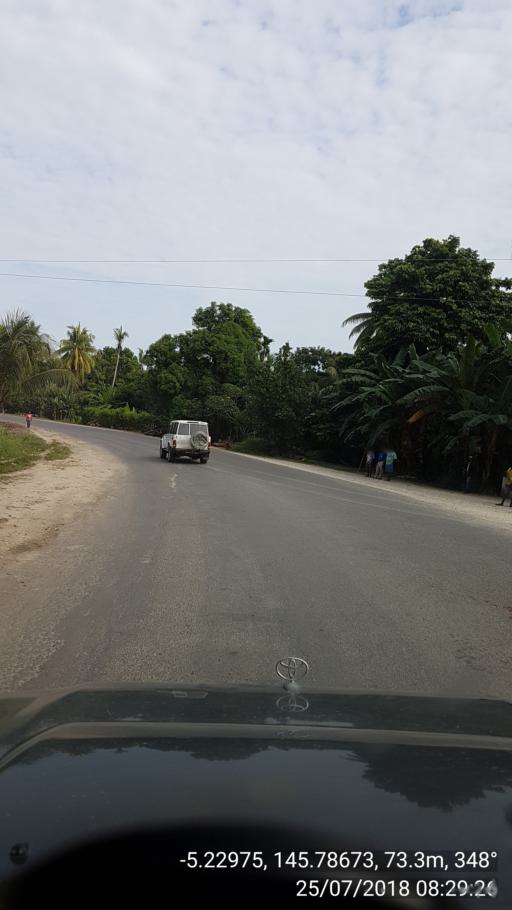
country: PG
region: Madang
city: Madang
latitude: -5.2297
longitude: 145.7867
